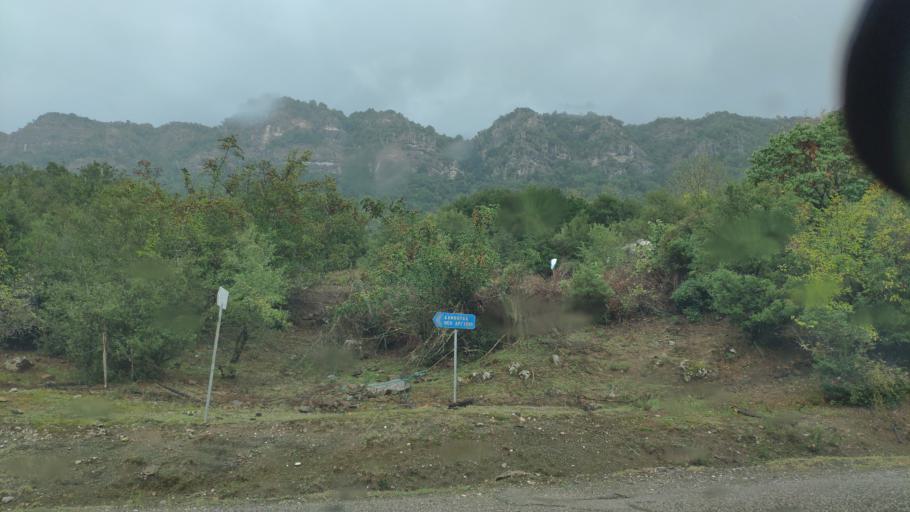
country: GR
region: Central Greece
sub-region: Nomos Evrytanias
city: Kerasochori
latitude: 39.1007
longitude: 21.4350
